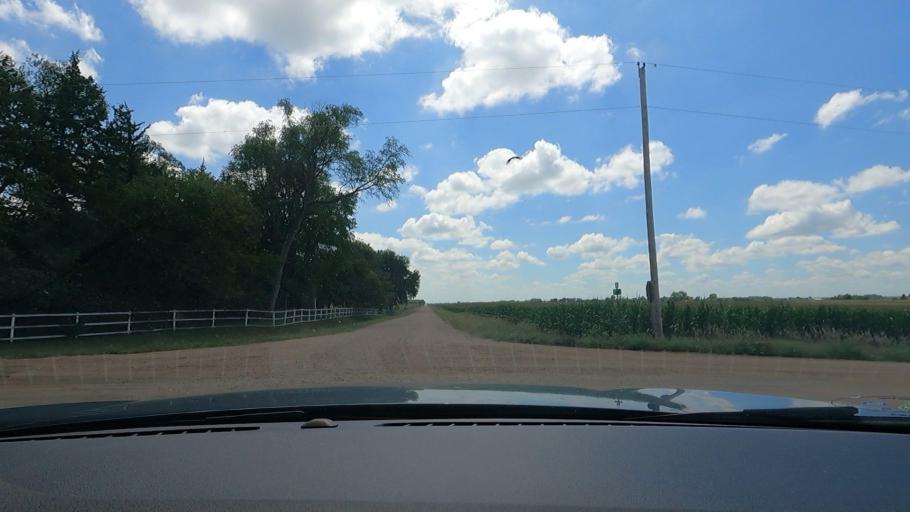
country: US
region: Nebraska
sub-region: Saunders County
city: Wahoo
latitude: 41.2784
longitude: -96.5419
